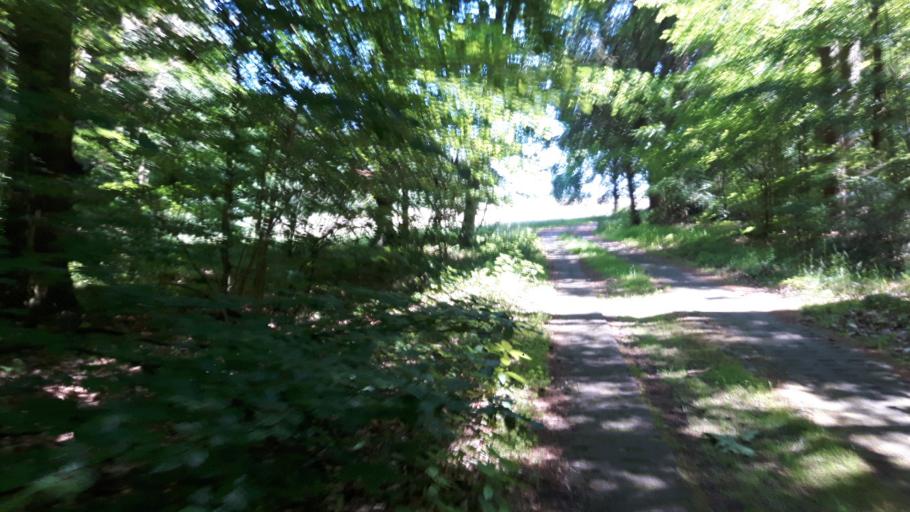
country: PL
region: Pomeranian Voivodeship
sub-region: Powiat slupski
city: Smoldzino
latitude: 54.6720
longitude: 17.1847
